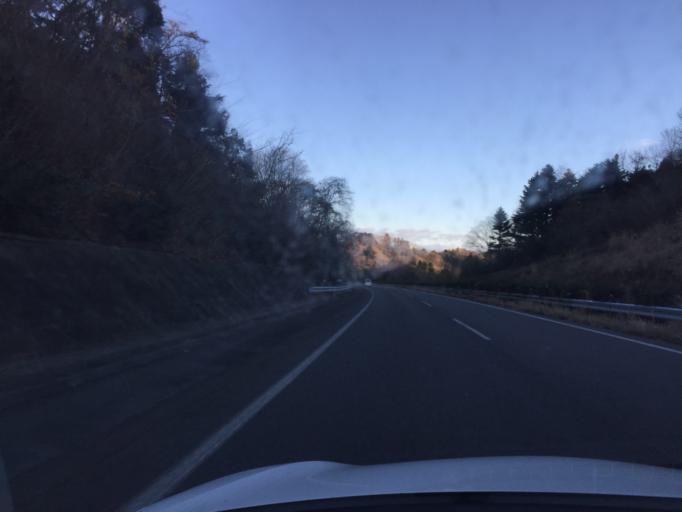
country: JP
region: Fukushima
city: Iwaki
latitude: 36.9711
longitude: 140.7920
